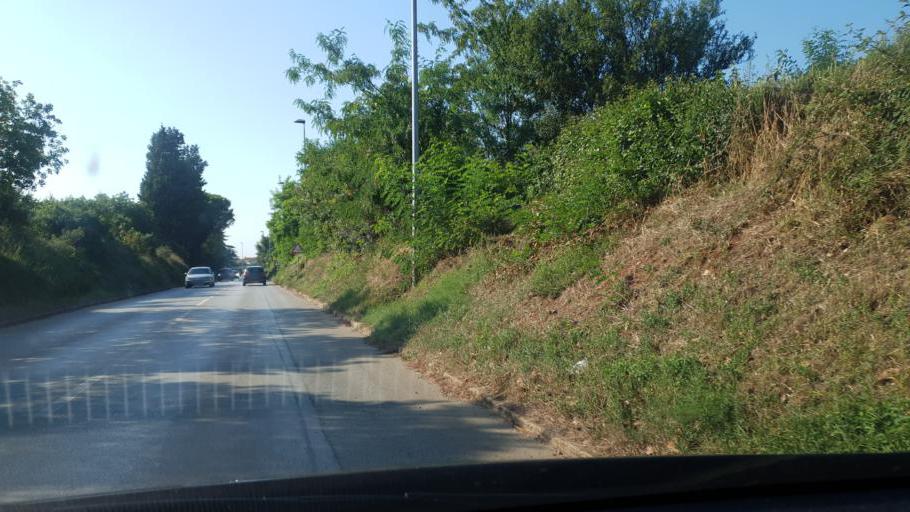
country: HR
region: Istarska
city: Fazana
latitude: 44.9119
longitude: 13.8196
